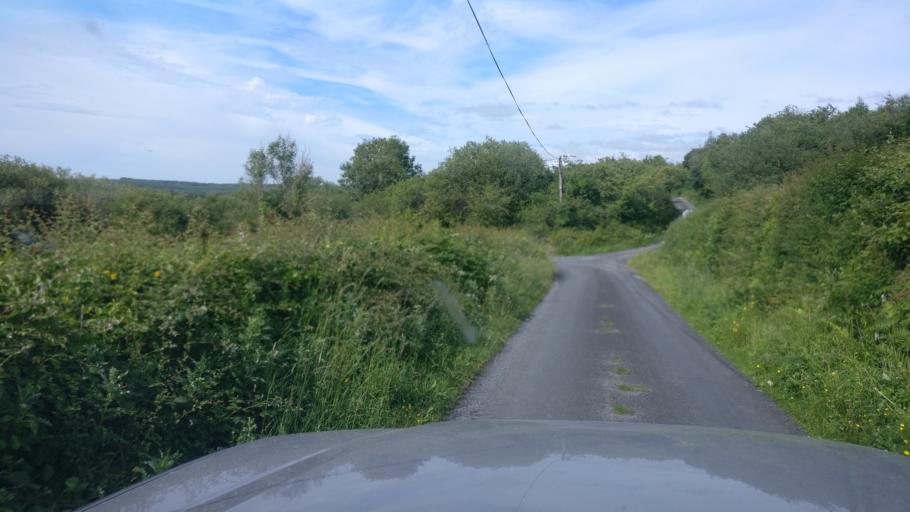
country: IE
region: Connaught
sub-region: County Galway
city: Gort
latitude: 53.0969
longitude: -8.6967
